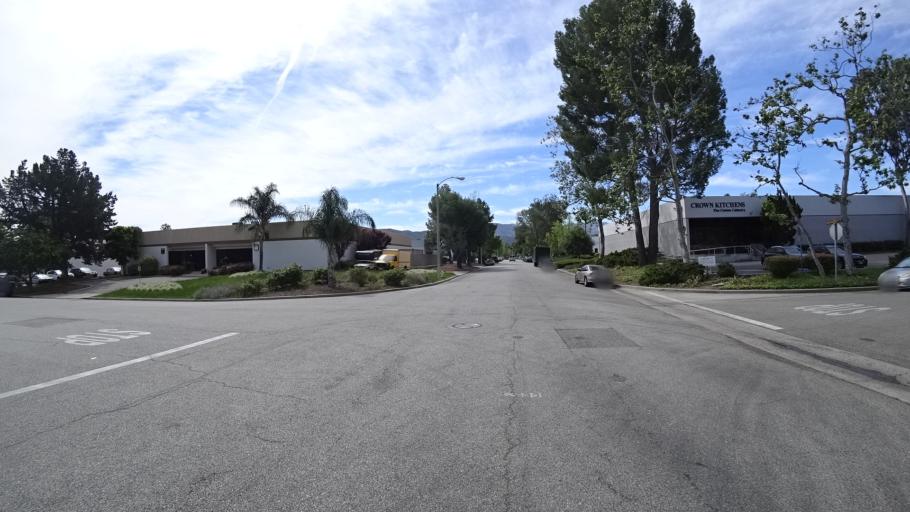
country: US
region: California
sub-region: Ventura County
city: Casa Conejo
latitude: 34.1929
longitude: -118.9315
